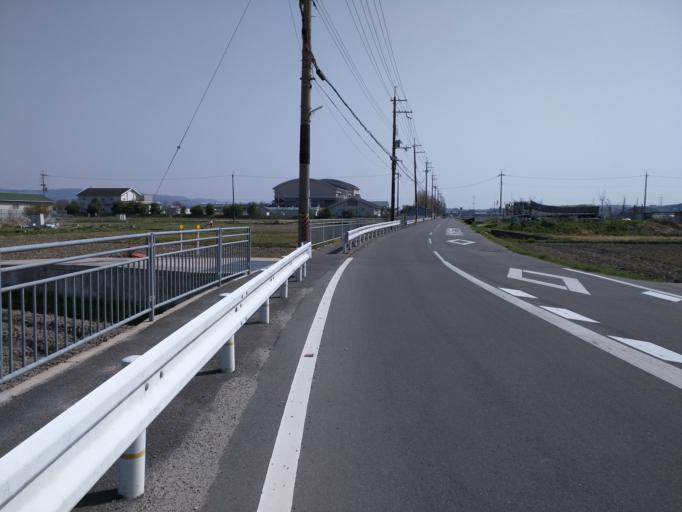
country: JP
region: Kyoto
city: Tanabe
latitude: 34.7788
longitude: 135.7976
